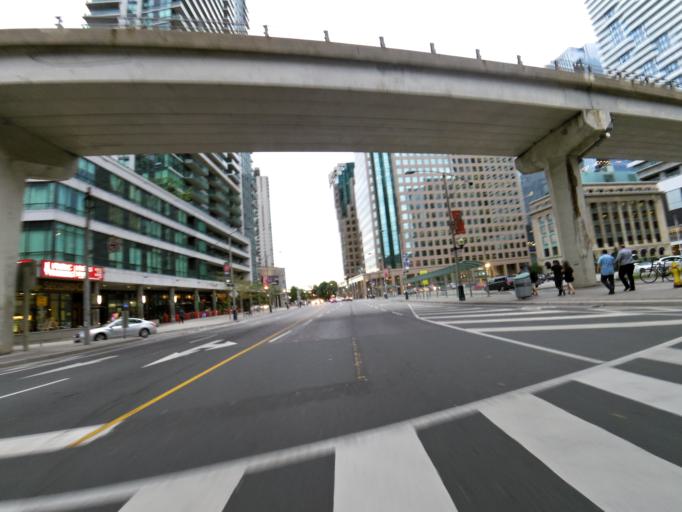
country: CA
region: Ontario
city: Toronto
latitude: 43.6430
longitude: -79.3779
